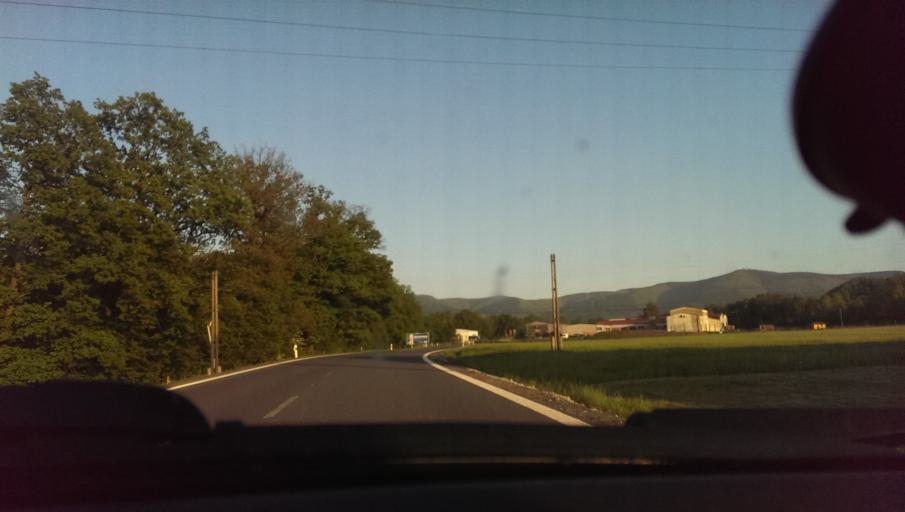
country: CZ
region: Moravskoslezsky
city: Frenstat pod Radhostem
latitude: 49.5604
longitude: 18.1953
